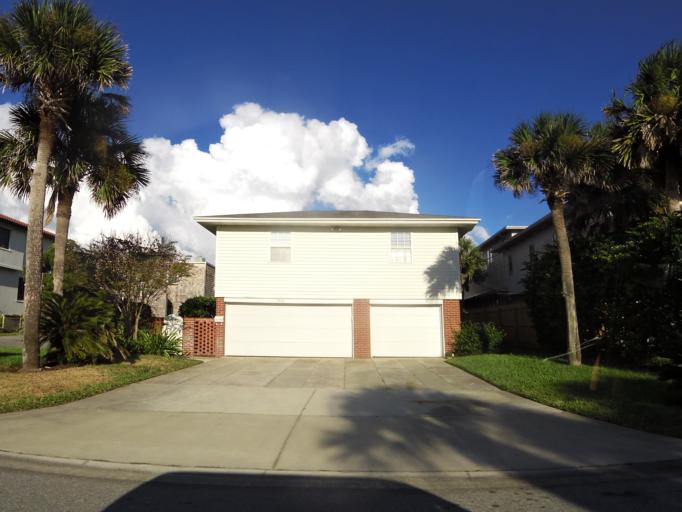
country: US
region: Florida
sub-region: Saint Johns County
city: Ponte Vedra Beach
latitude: 30.2596
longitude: -81.3831
